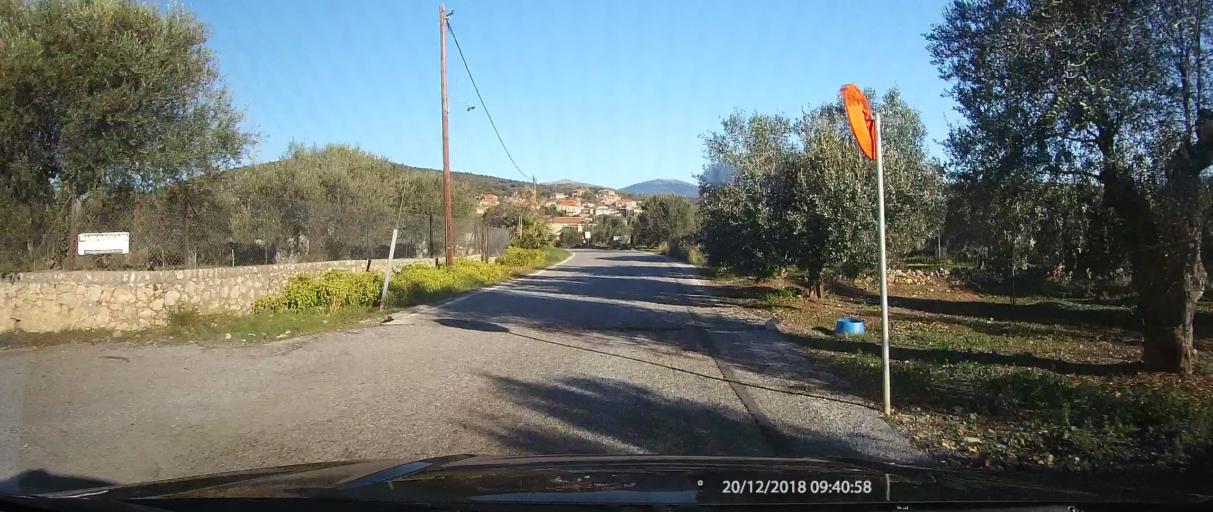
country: GR
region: Peloponnese
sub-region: Nomos Lakonias
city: Yerakion
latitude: 36.9497
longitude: 22.7661
